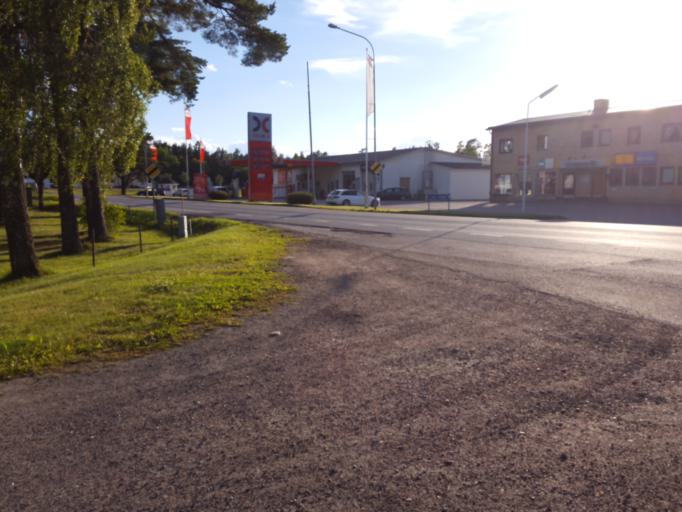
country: SE
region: Uppsala
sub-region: Osthammars Kommun
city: OEsthammar
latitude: 60.2559
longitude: 18.3488
